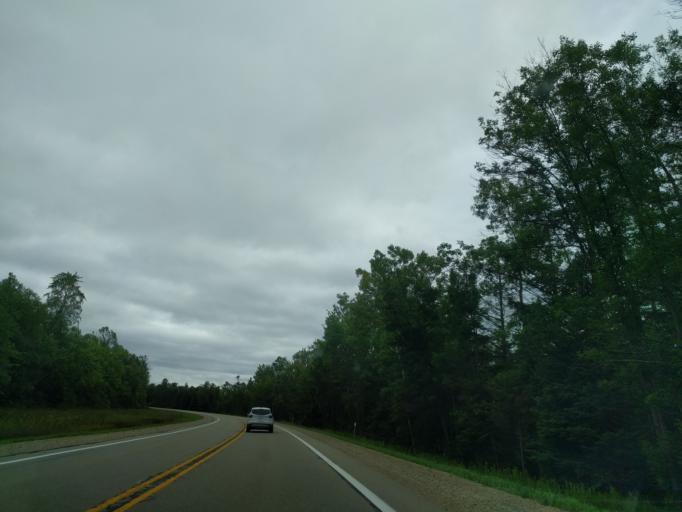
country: US
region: Michigan
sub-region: Menominee County
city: Menominee
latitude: 45.4301
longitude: -87.3517
